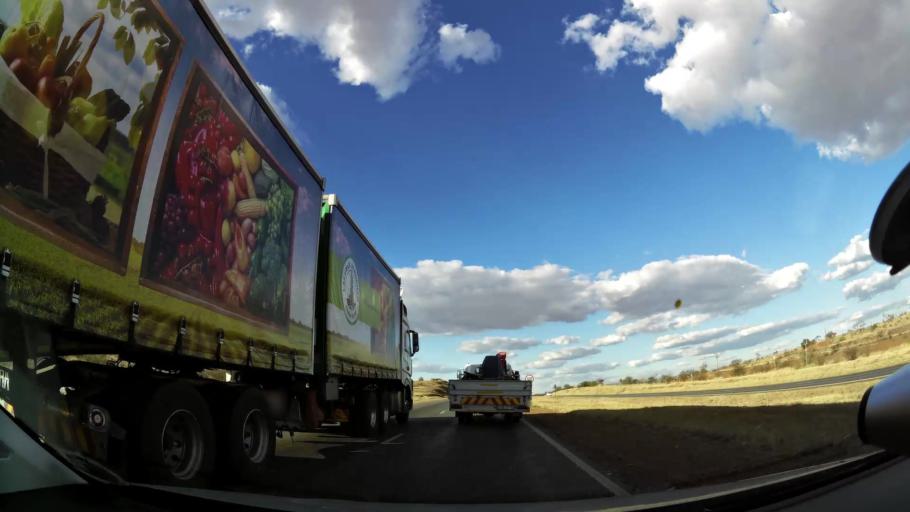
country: ZA
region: North-West
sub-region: Dr Kenneth Kaunda District Municipality
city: Potchefstroom
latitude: -26.7575
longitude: 26.9928
